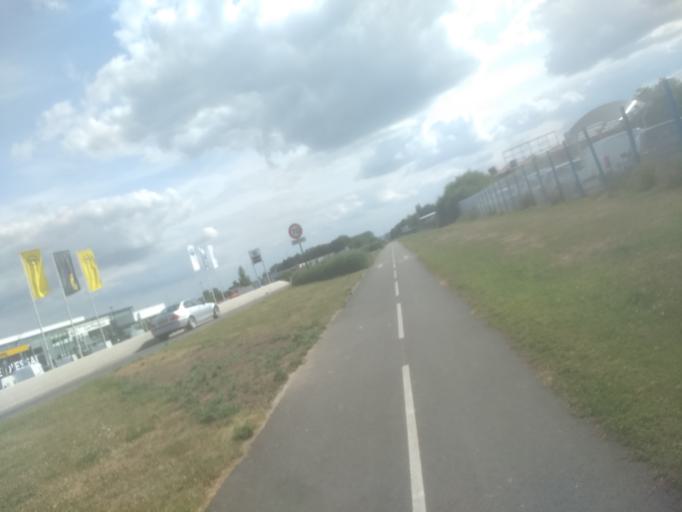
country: FR
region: Nord-Pas-de-Calais
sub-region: Departement du Pas-de-Calais
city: Beaurains
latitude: 50.2661
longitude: 2.7963
